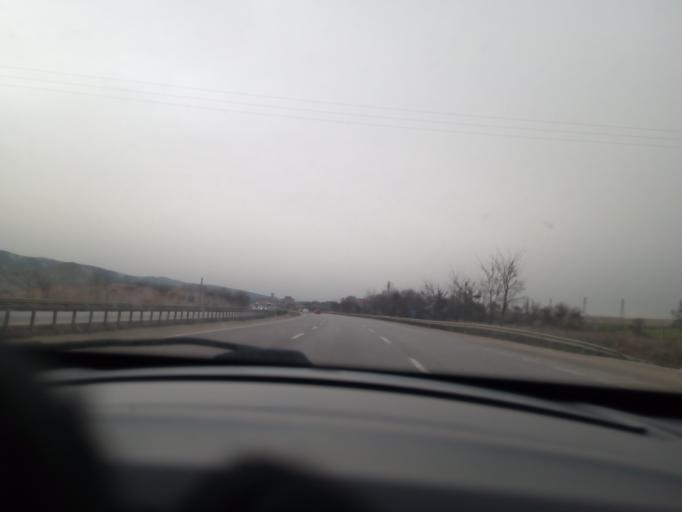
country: TR
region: Balikesir
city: Susurluk
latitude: 39.9634
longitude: 28.1702
